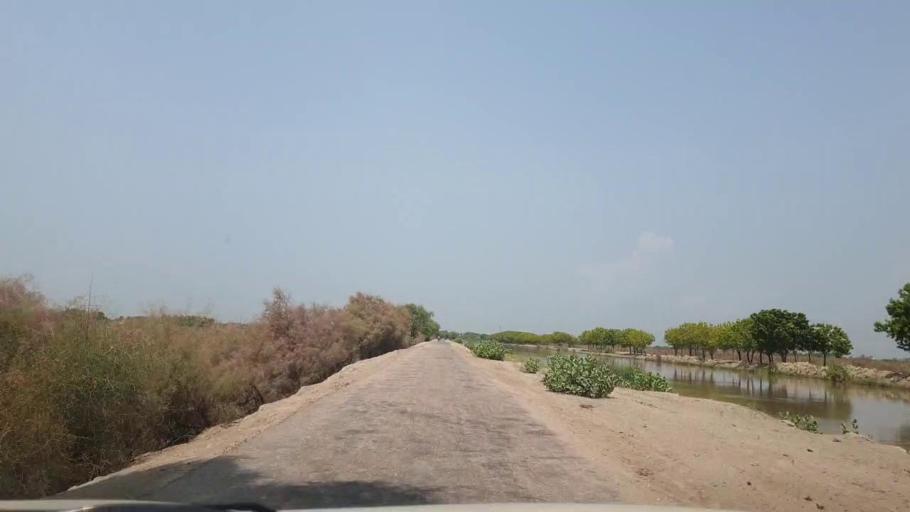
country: PK
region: Sindh
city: Dokri
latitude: 27.3490
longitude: 68.1121
